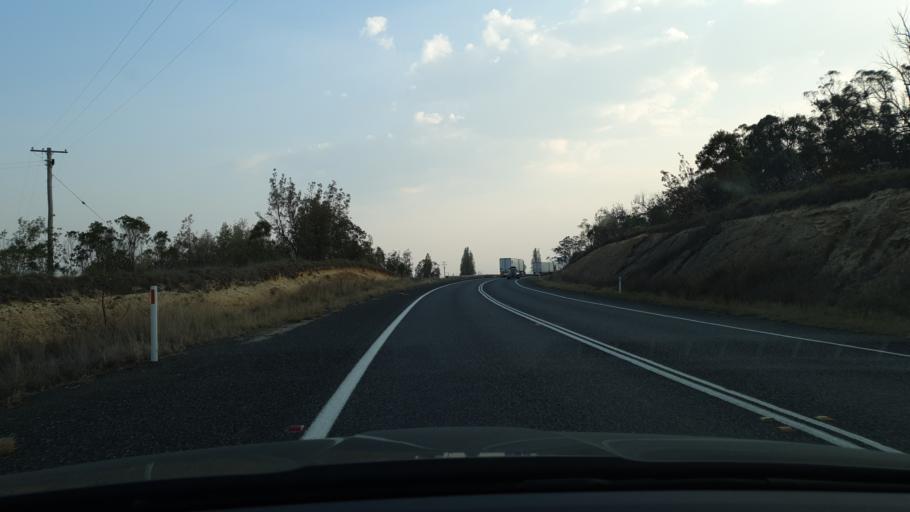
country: AU
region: New South Wales
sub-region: Tenterfield Municipality
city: Carrolls Creek
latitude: -29.1718
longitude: 152.0074
